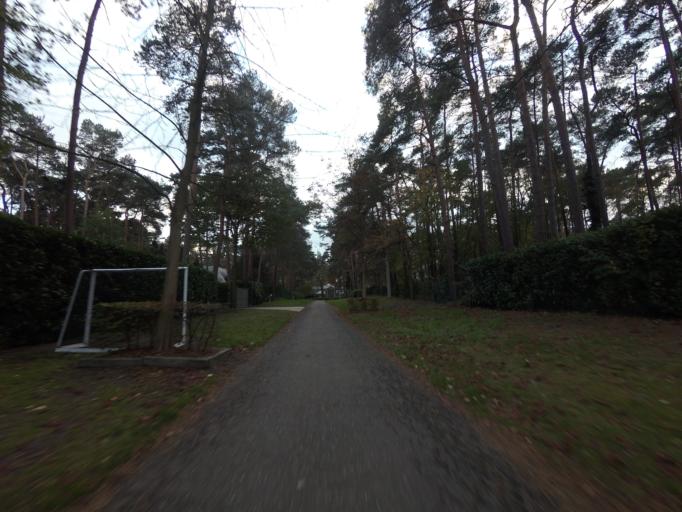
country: BE
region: Flanders
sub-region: Provincie Antwerpen
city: Bonheiden
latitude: 51.0204
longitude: 4.5818
